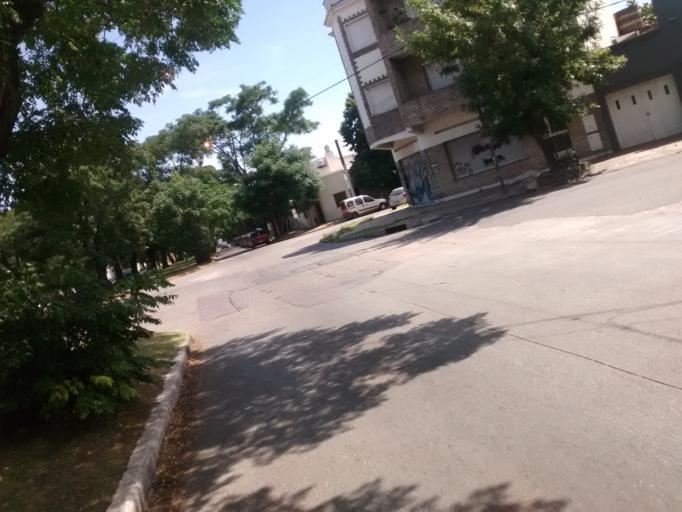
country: AR
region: Buenos Aires
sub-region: Partido de La Plata
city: La Plata
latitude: -34.8968
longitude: -57.9561
